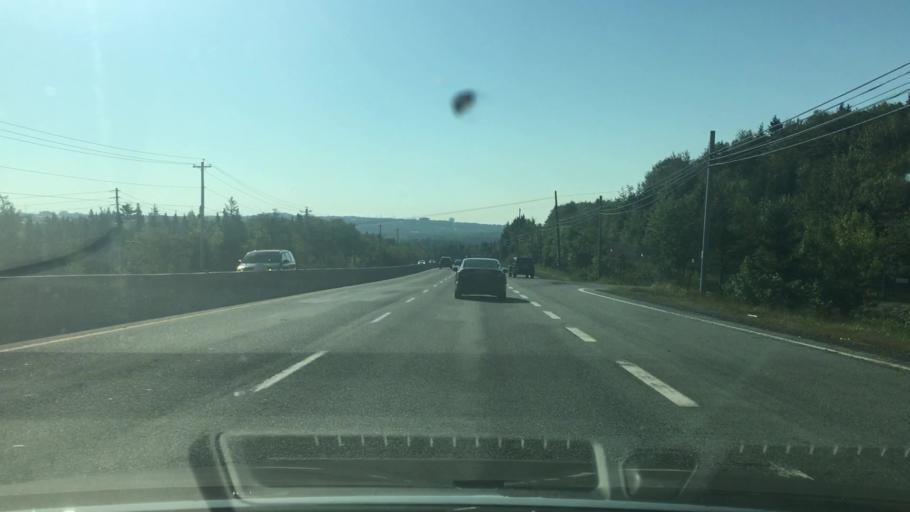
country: CA
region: Nova Scotia
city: Dartmouth
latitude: 44.7128
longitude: -63.6292
